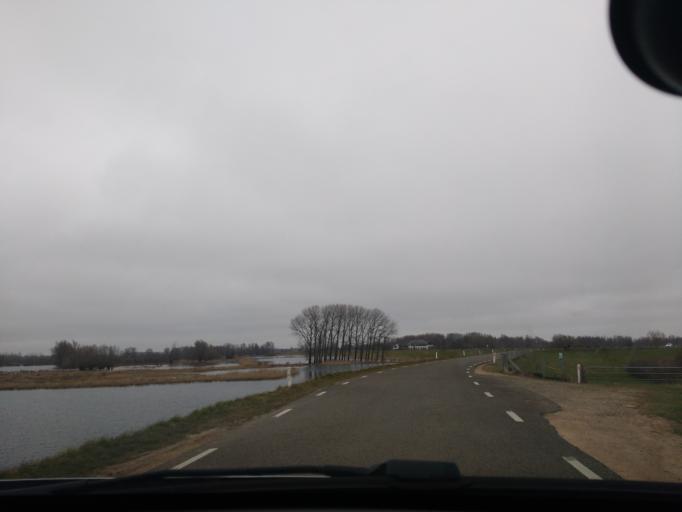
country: NL
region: Gelderland
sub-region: Gemeente Groesbeek
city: Berg en Dal
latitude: 51.8540
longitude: 5.8986
